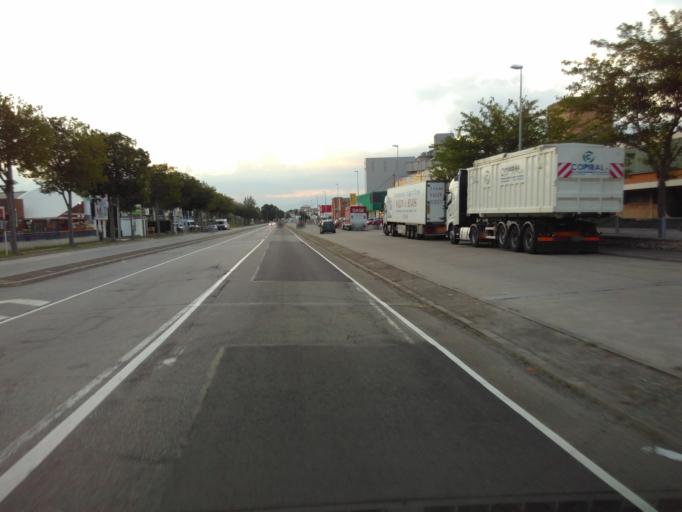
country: ES
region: Catalonia
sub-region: Provincia de Barcelona
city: Vic
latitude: 41.9414
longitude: 2.2538
